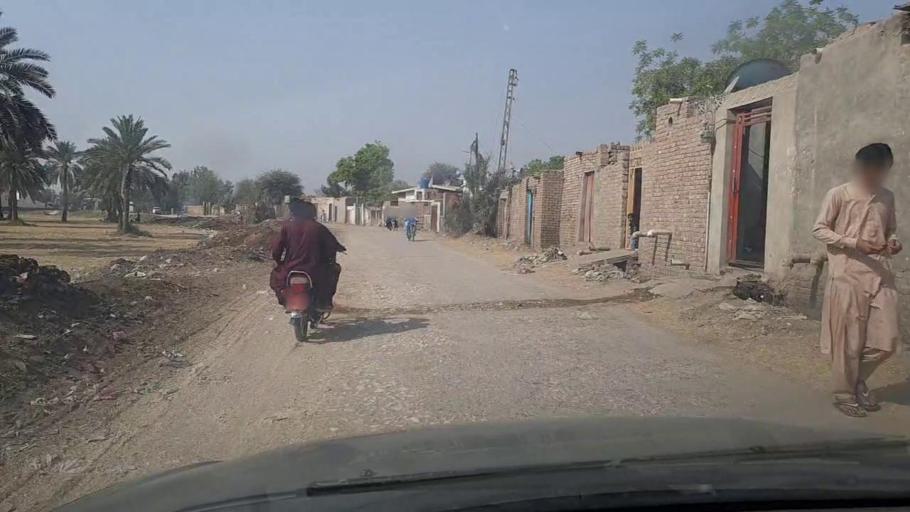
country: PK
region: Sindh
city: Mirpur Mathelo
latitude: 28.0156
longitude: 69.5480
